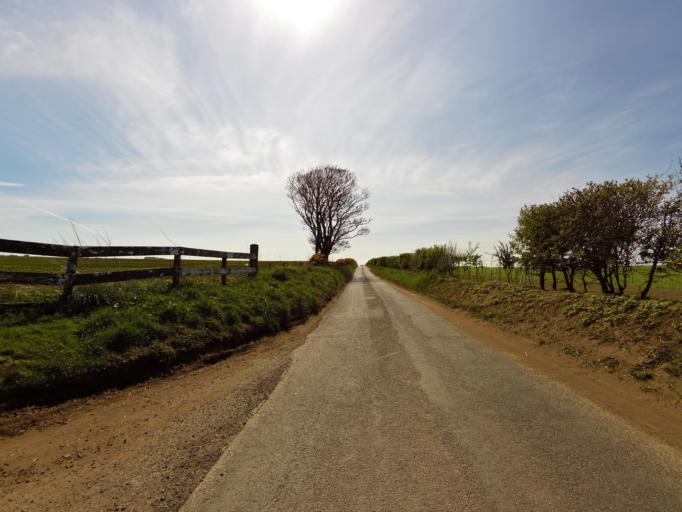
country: GB
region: Scotland
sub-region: Angus
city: Montrose
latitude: 56.6429
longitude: -2.5162
